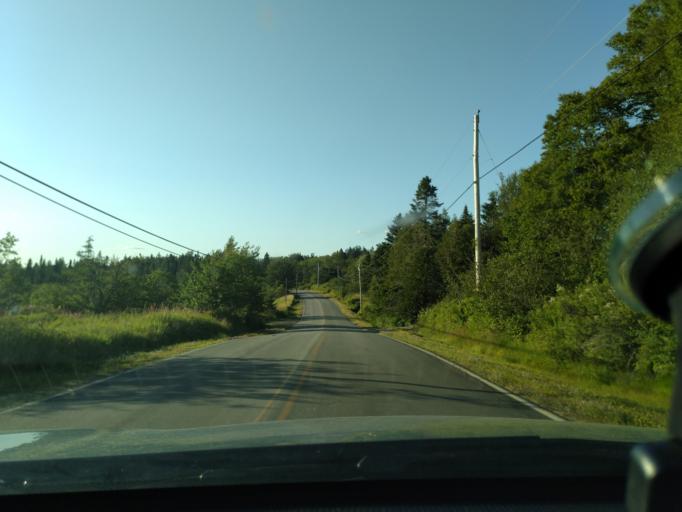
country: US
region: Maine
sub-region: Washington County
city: Machiasport
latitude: 44.6647
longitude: -67.2378
